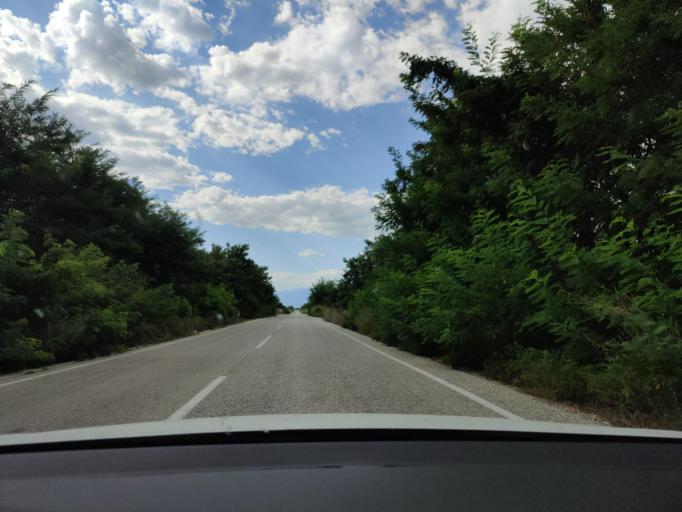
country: GR
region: Central Macedonia
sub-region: Nomos Serron
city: Strymoniko
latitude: 41.0693
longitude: 23.3027
